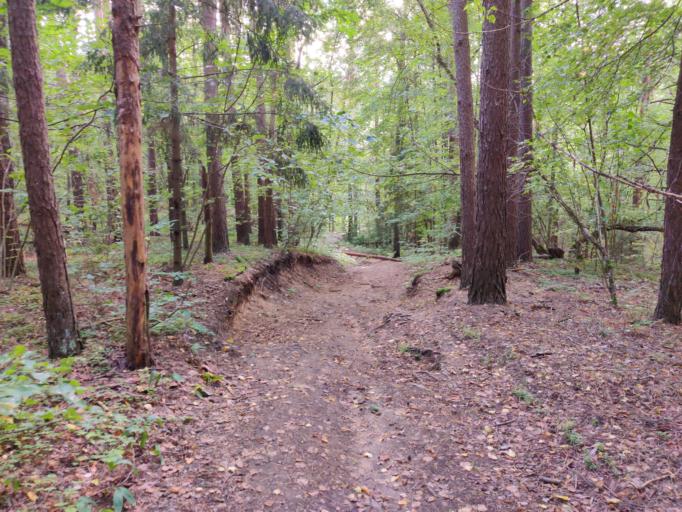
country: LT
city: Trakai
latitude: 54.7435
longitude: 24.9744
